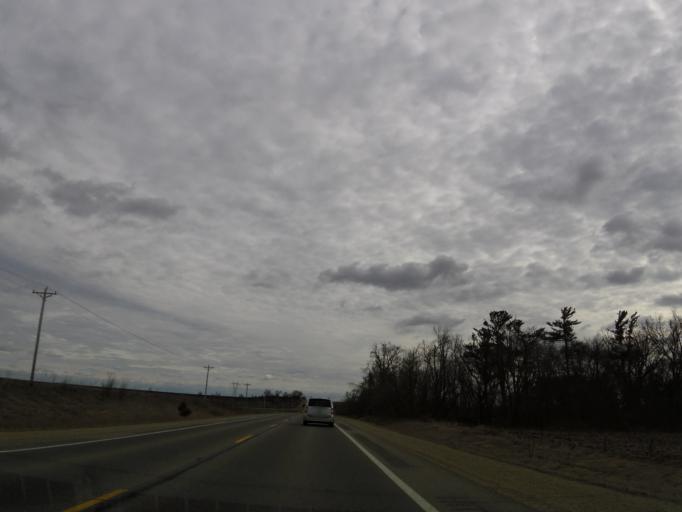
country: US
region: Iowa
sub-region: Chickasaw County
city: New Hampton
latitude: 43.1164
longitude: -92.2980
